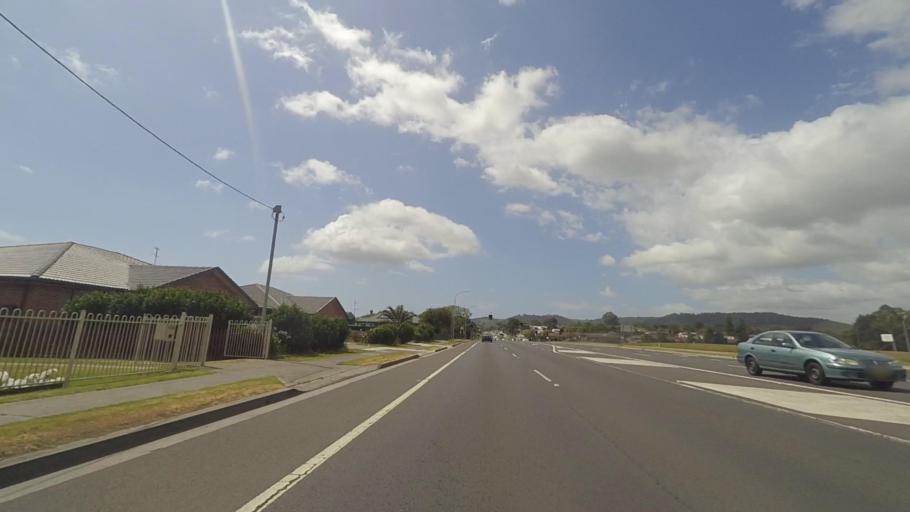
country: AU
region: New South Wales
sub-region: Shellharbour
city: Albion Park Rail
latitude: -34.5622
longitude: 150.7971
